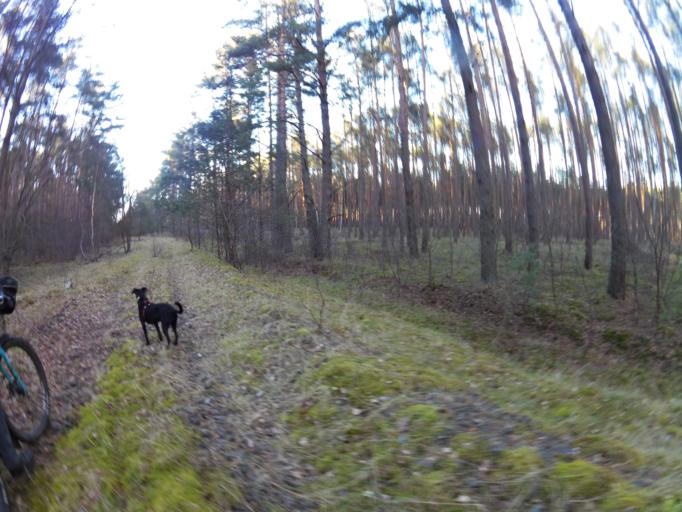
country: PL
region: West Pomeranian Voivodeship
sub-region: Powiat mysliborski
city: Debno
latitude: 52.8298
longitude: 14.7729
